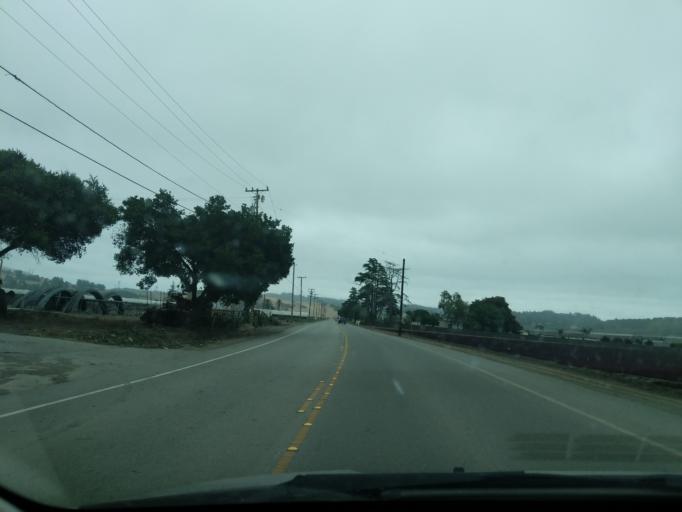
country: US
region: California
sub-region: San Benito County
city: Aromas
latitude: 36.8983
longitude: -121.6853
